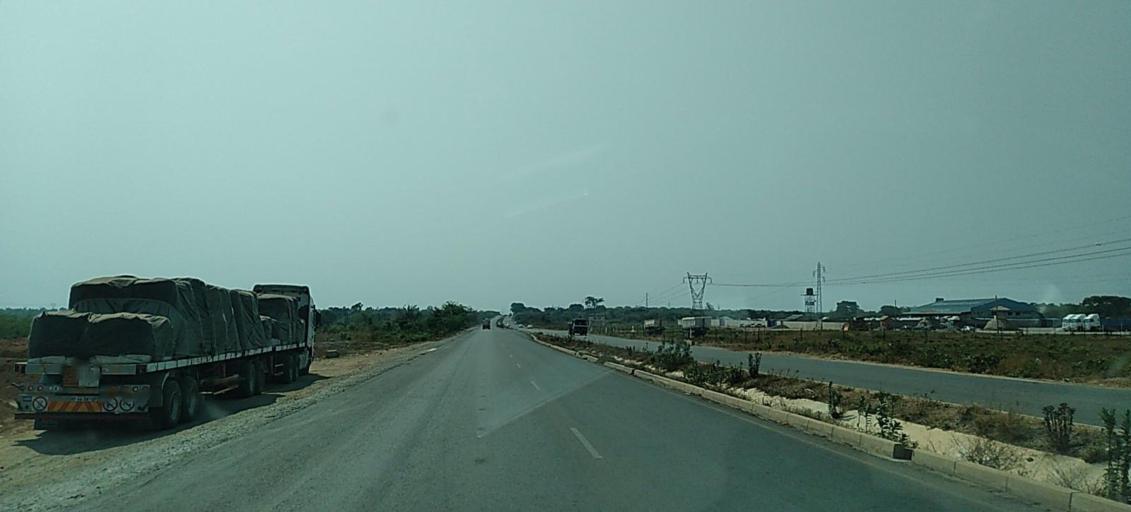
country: ZM
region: Copperbelt
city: Chingola
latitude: -12.5747
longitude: 27.9161
